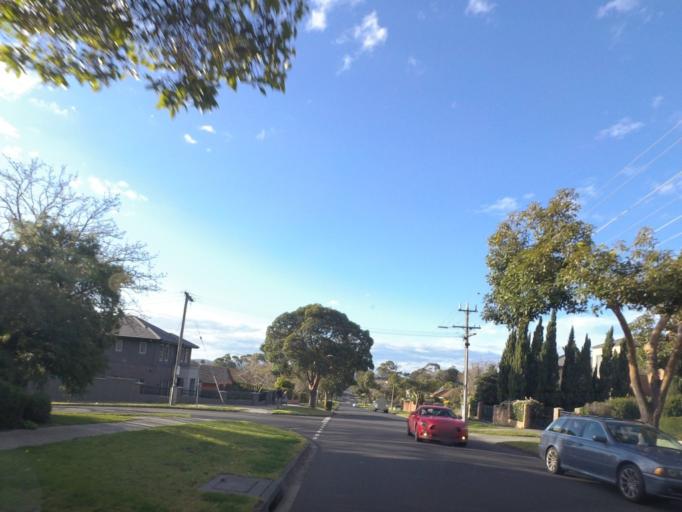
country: AU
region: Victoria
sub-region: Boroondara
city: Balwyn North
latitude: -37.7922
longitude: 145.0853
